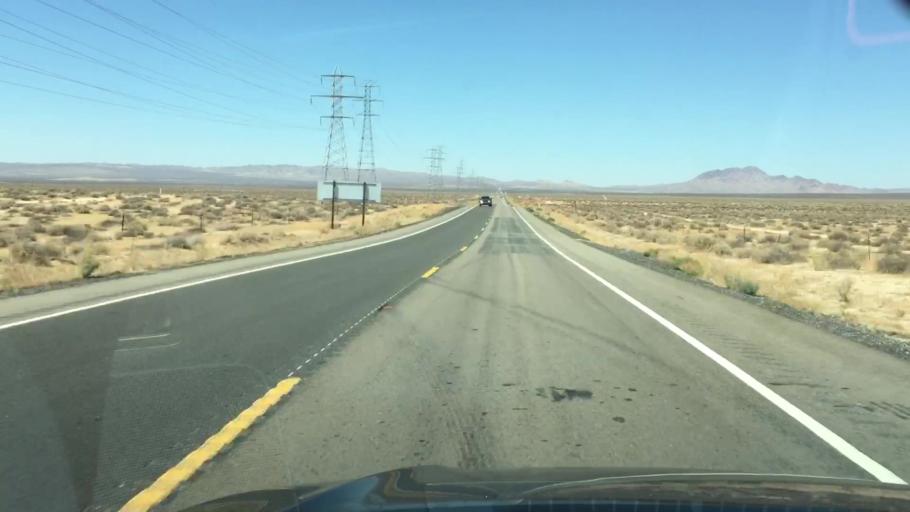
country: US
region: California
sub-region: Kern County
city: Boron
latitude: 35.1664
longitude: -117.5900
